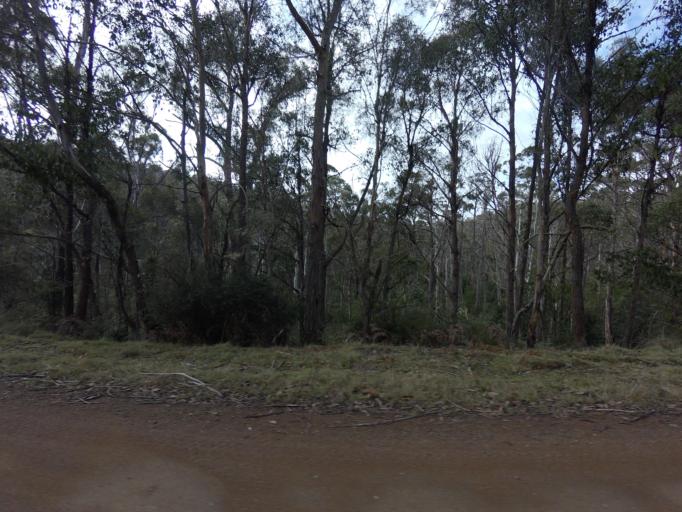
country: AU
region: Tasmania
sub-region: Derwent Valley
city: New Norfolk
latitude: -42.7495
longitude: 146.8696
